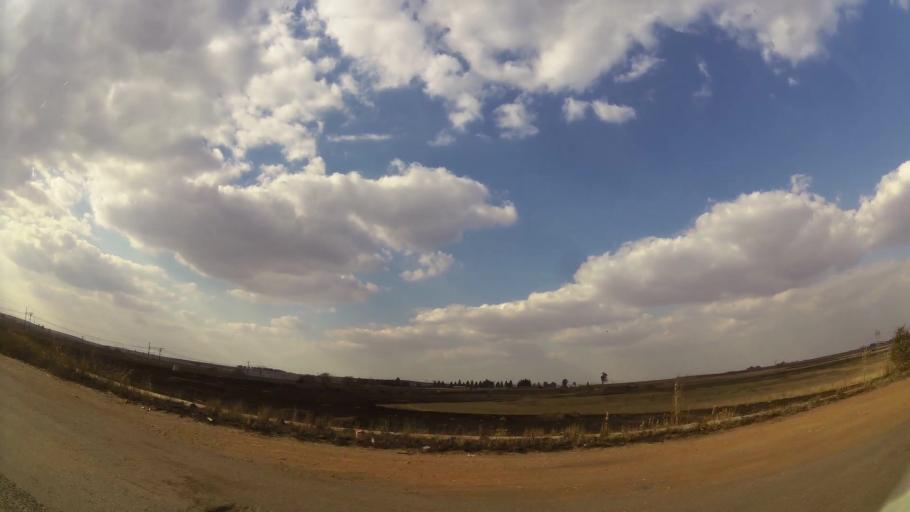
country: ZA
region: Mpumalanga
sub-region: Nkangala District Municipality
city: Delmas
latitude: -26.1513
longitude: 28.6963
